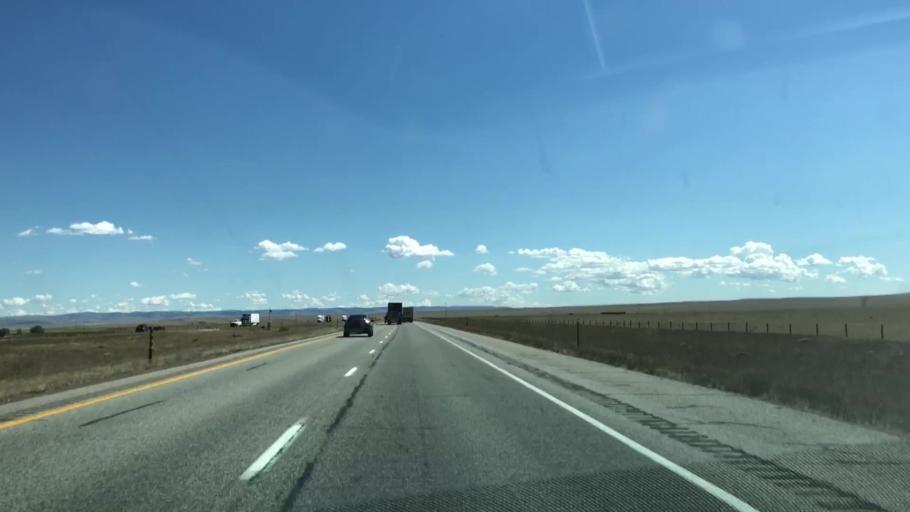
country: US
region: Wyoming
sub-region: Albany County
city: Laramie
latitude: 41.3783
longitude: -105.8064
